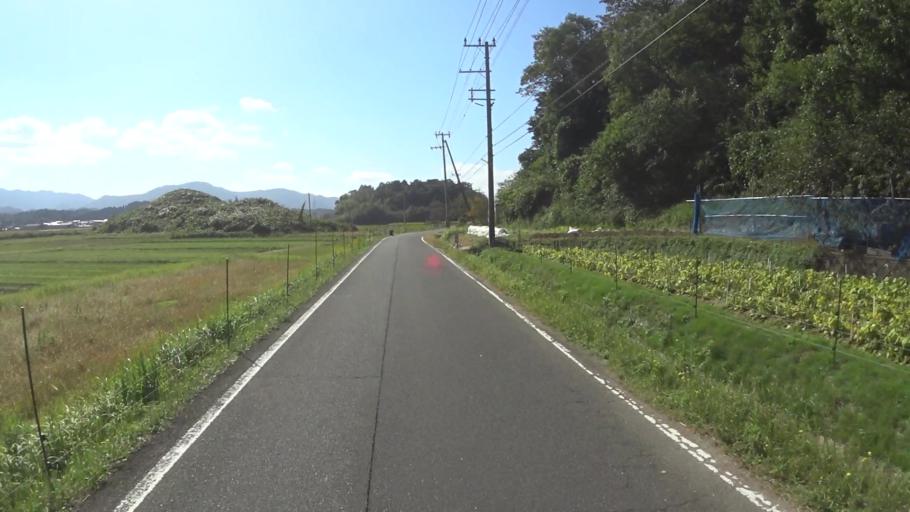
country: JP
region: Kyoto
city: Miyazu
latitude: 35.6864
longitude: 135.0935
